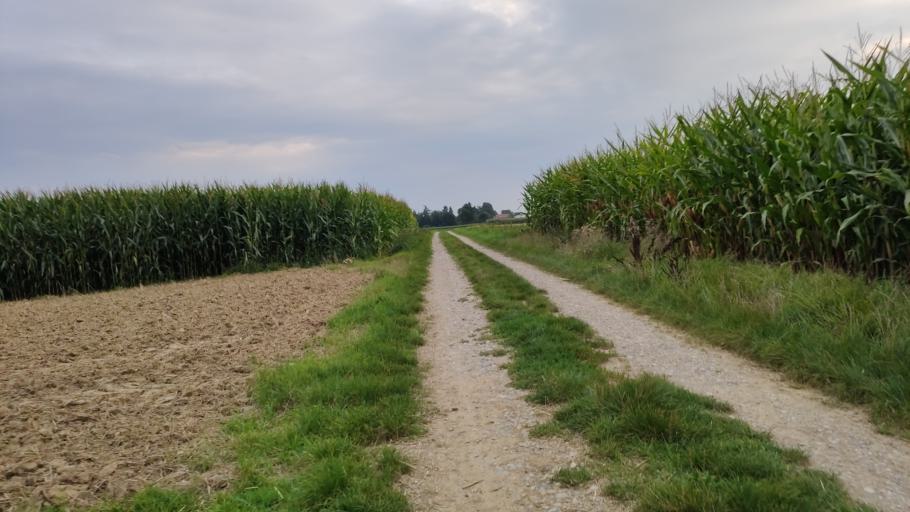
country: DE
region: Bavaria
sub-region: Swabia
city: Oberottmarshausen
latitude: 48.2453
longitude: 10.8599
